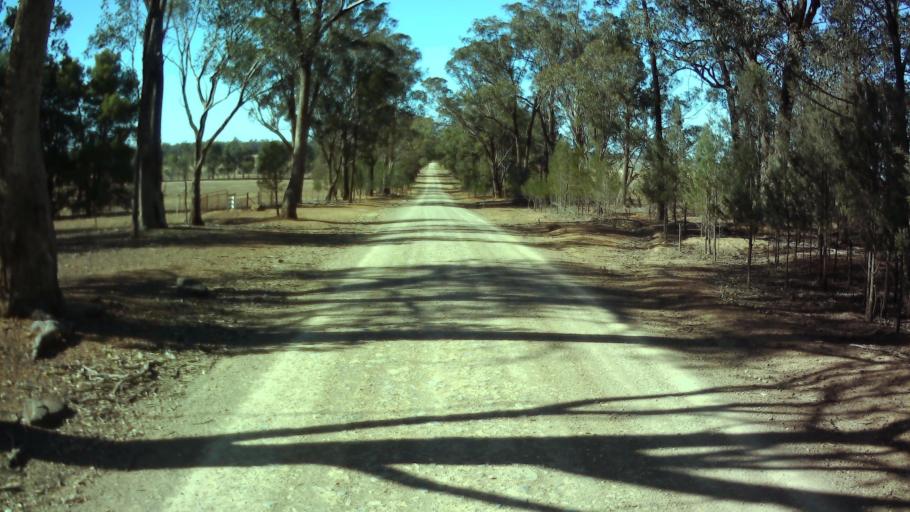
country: AU
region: New South Wales
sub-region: Weddin
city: Grenfell
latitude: -33.9275
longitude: 147.8736
